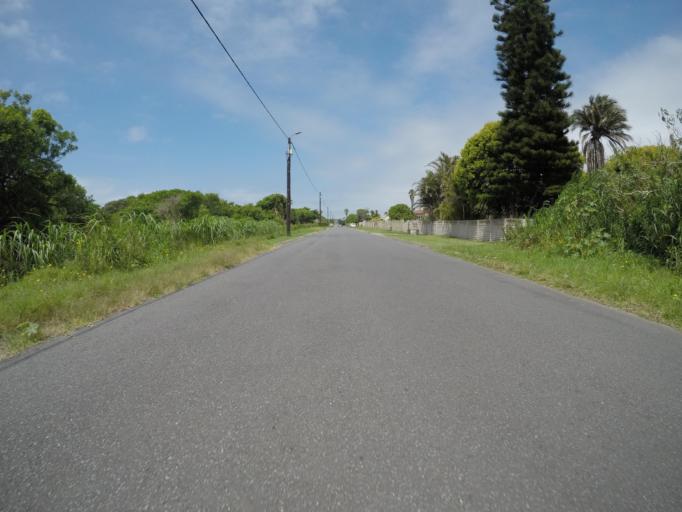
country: ZA
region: Eastern Cape
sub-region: Buffalo City Metropolitan Municipality
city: East London
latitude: -32.9440
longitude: 28.0217
